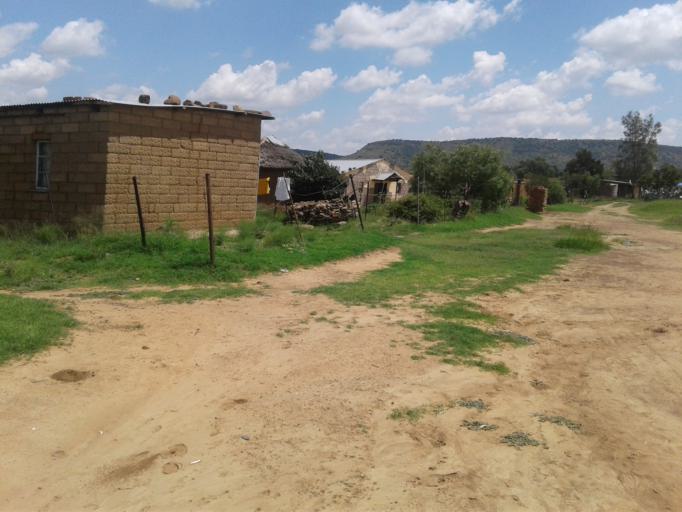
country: LS
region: Mafeteng
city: Mafeteng
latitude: -29.7578
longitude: 27.1109
